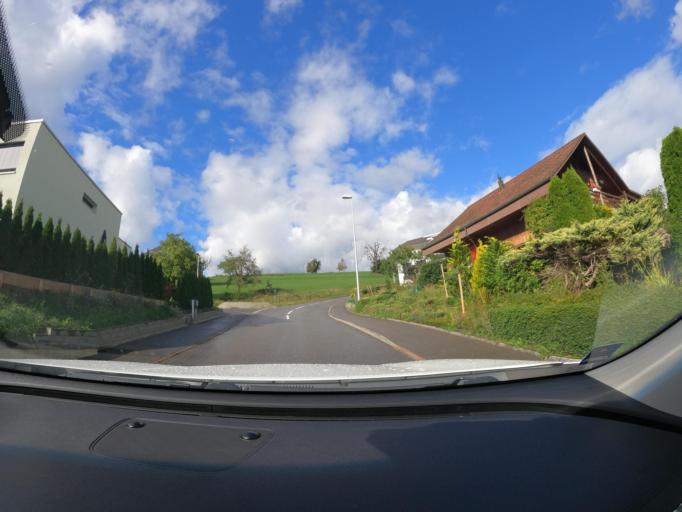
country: CH
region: Aargau
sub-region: Bezirk Kulm
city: Gontenschwil
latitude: 47.2891
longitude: 8.1526
